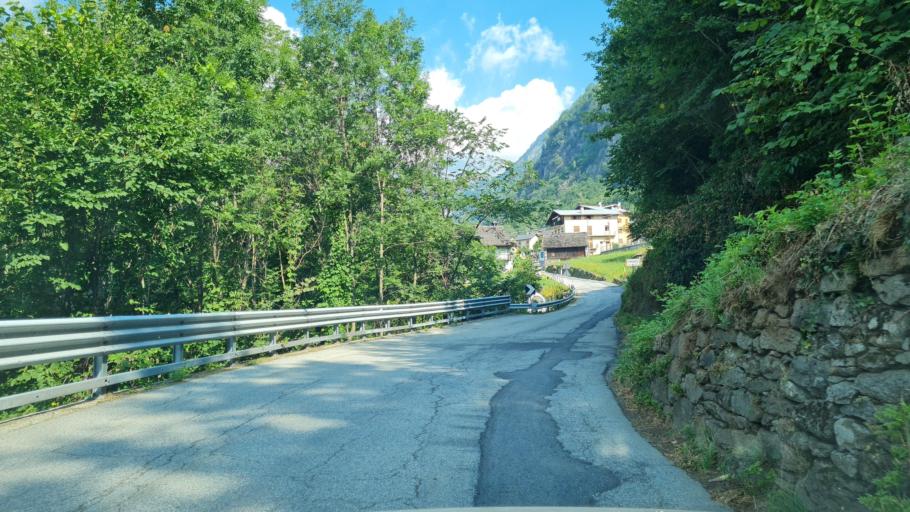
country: IT
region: Piedmont
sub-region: Provincia Verbano-Cusio-Ossola
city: Baceno
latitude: 46.2687
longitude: 8.3099
